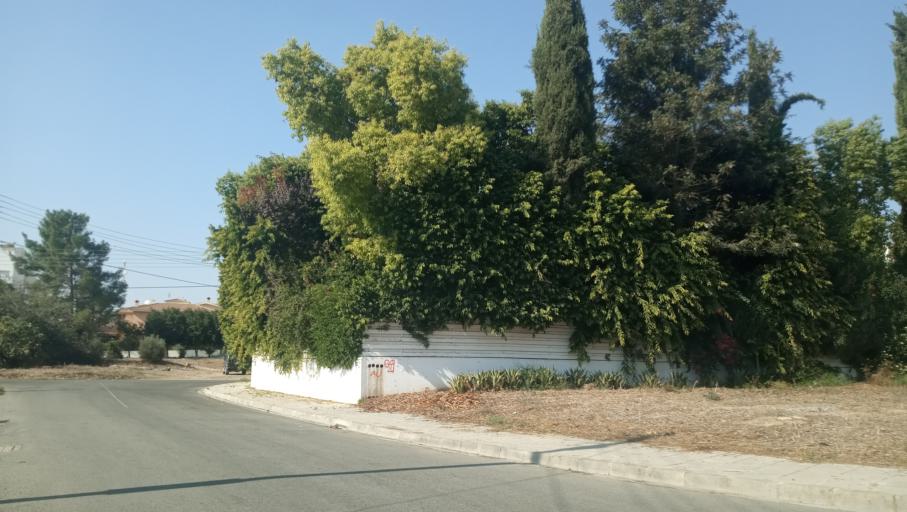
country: CY
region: Lefkosia
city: Nicosia
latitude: 35.1469
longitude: 33.3901
